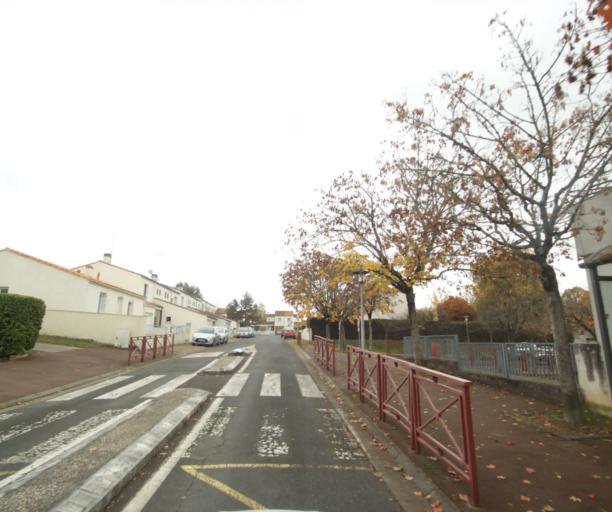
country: FR
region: Poitou-Charentes
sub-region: Departement de la Charente-Maritime
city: Saintes
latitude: 45.7342
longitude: -0.6517
